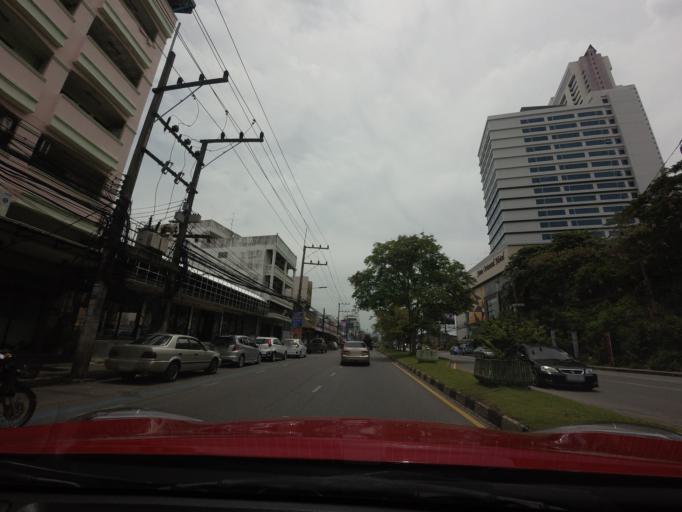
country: TH
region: Songkhla
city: Hat Yai
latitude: 6.9983
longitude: 100.4816
